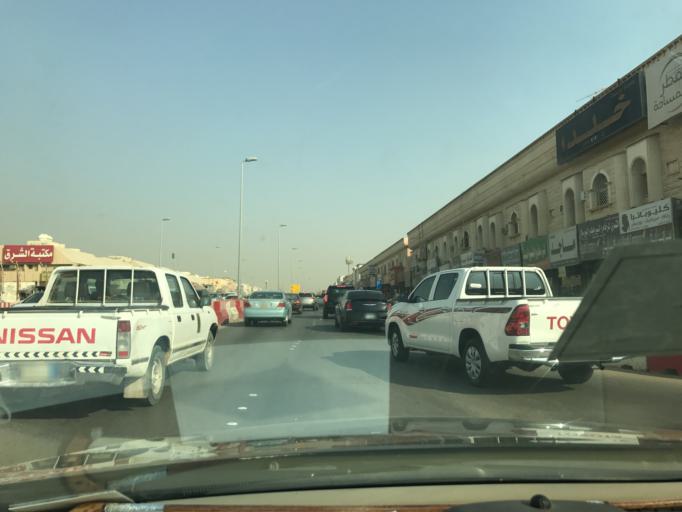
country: SA
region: Ar Riyad
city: Riyadh
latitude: 24.7544
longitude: 46.7691
